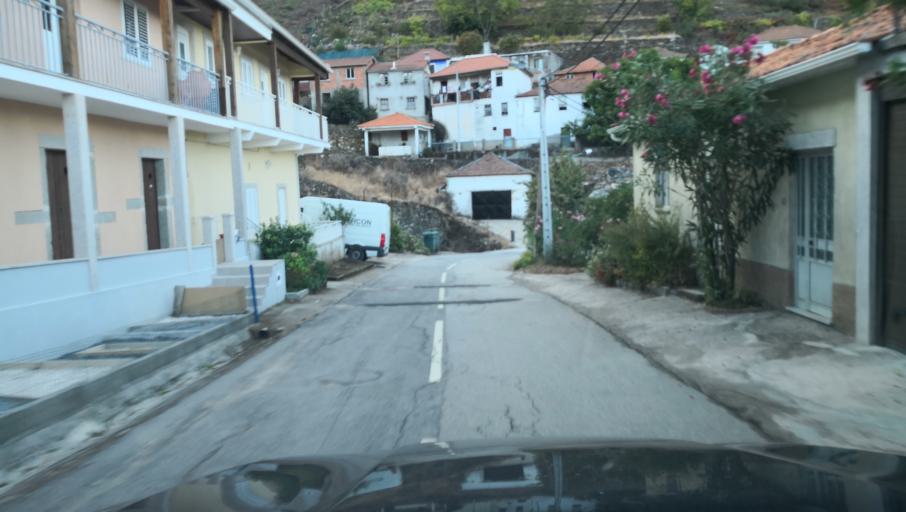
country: PT
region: Vila Real
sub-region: Santa Marta de Penaguiao
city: Santa Marta de Penaguiao
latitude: 41.2476
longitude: -7.8439
